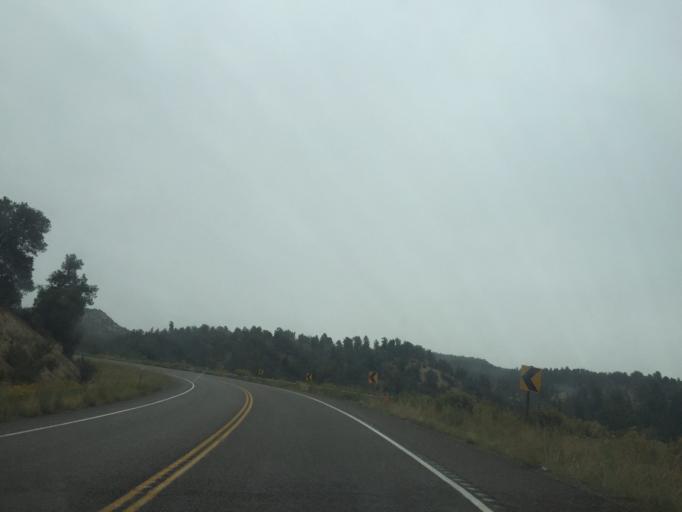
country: US
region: Utah
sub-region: Kane County
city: Kanab
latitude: 37.2046
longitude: -112.6852
